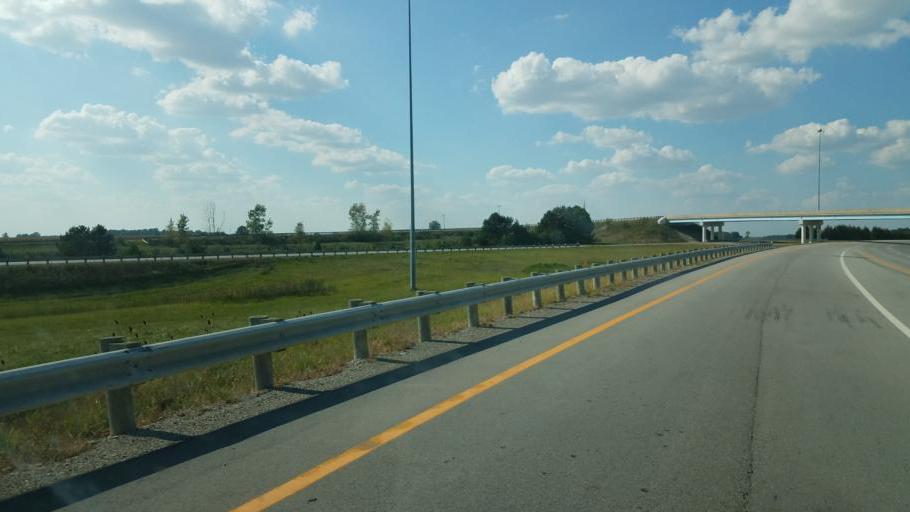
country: US
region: Ohio
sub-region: Wyandot County
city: Upper Sandusky
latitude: 40.8602
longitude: -83.3208
